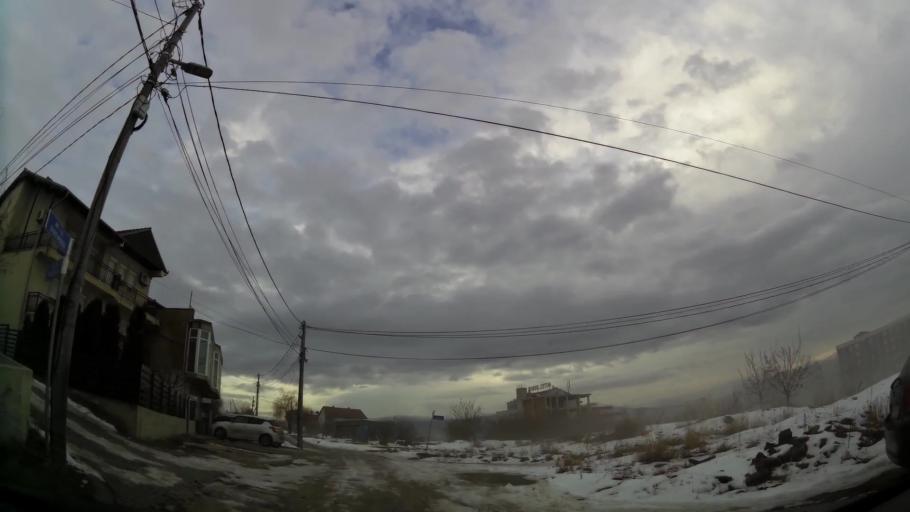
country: XK
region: Pristina
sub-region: Komuna e Prishtines
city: Pristina
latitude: 42.6609
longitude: 21.1470
